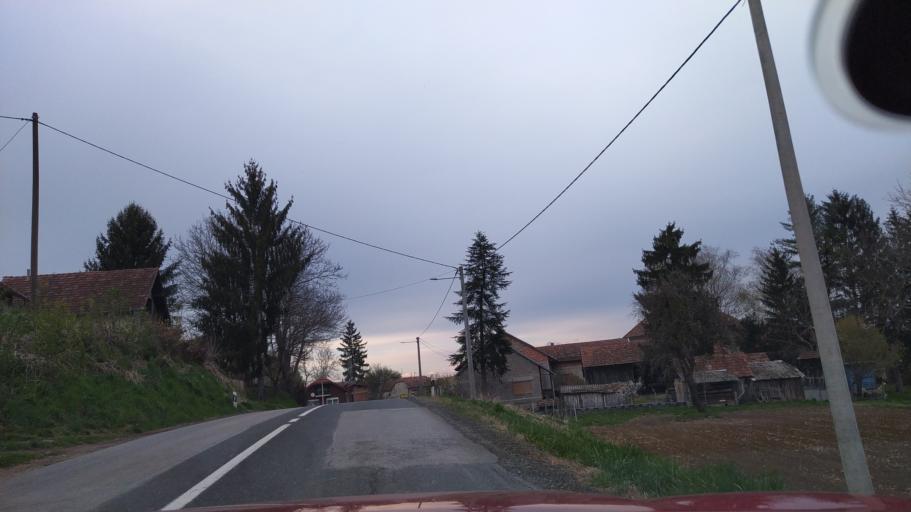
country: HR
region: Varazdinska
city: Ludbreg
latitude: 46.2311
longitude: 16.5454
